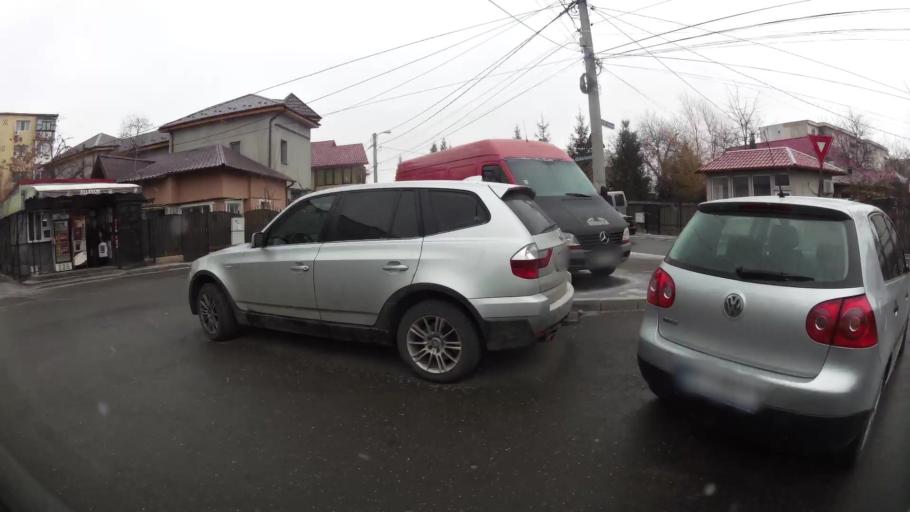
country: RO
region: Prahova
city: Ploiesti
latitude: 44.9403
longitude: 26.0465
